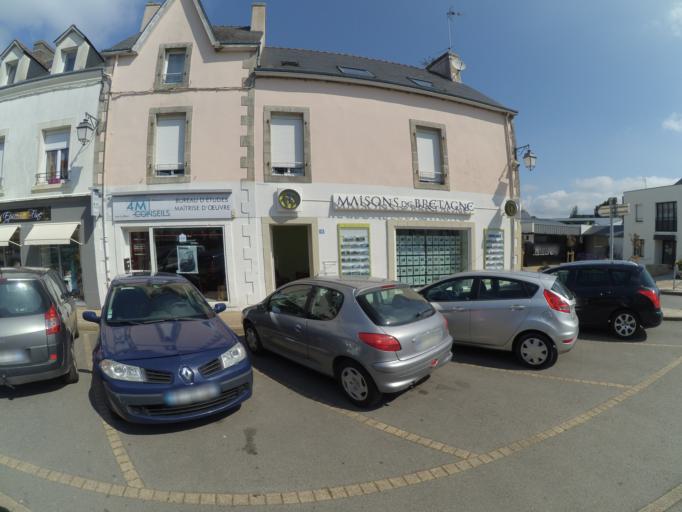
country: FR
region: Brittany
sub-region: Departement du Finistere
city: Bannalec
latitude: 47.9324
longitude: -3.6967
